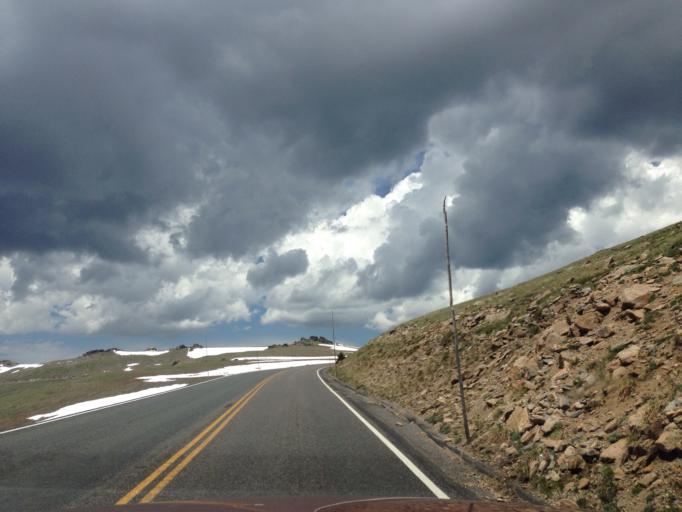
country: US
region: Colorado
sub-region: Larimer County
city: Estes Park
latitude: 40.4057
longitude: -105.7154
